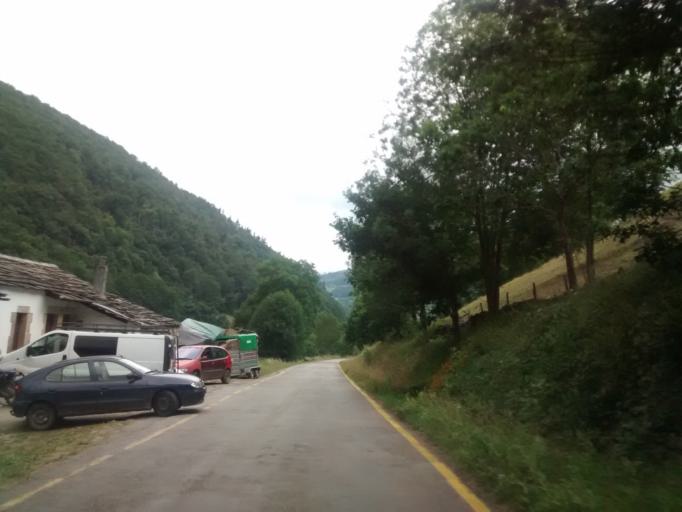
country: ES
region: Cantabria
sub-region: Provincia de Cantabria
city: Vega de Pas
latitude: 43.1511
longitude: -3.7764
